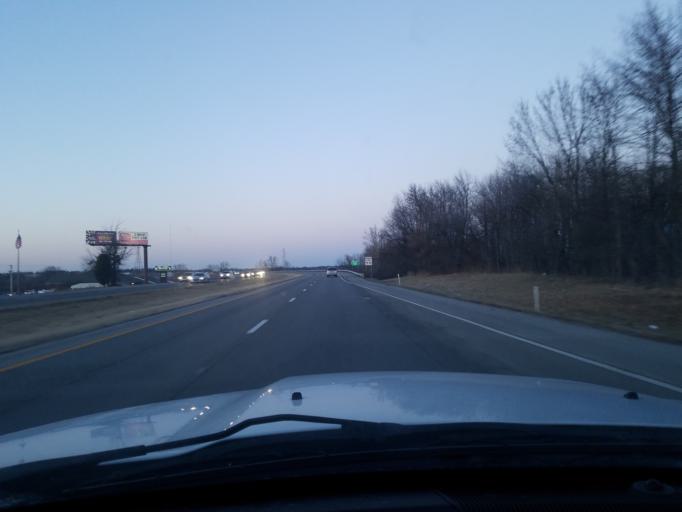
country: US
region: Kentucky
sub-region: Henderson County
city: Henderson
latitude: 37.8358
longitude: -87.5649
